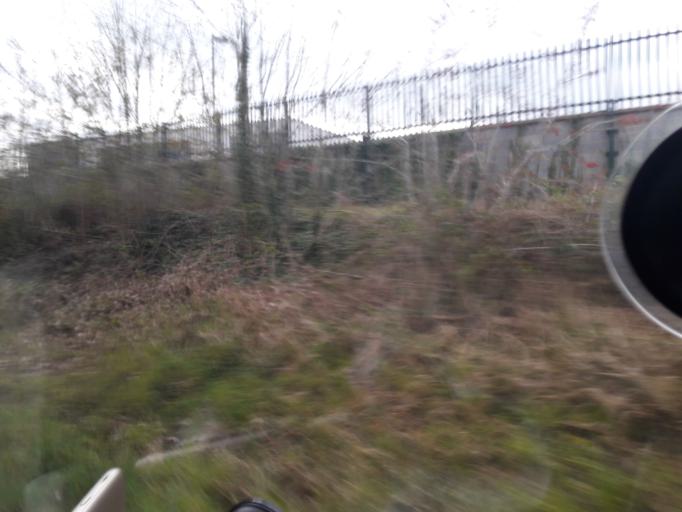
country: IE
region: Leinster
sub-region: An Iarmhi
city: An Muileann gCearr
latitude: 53.5308
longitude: -7.3473
